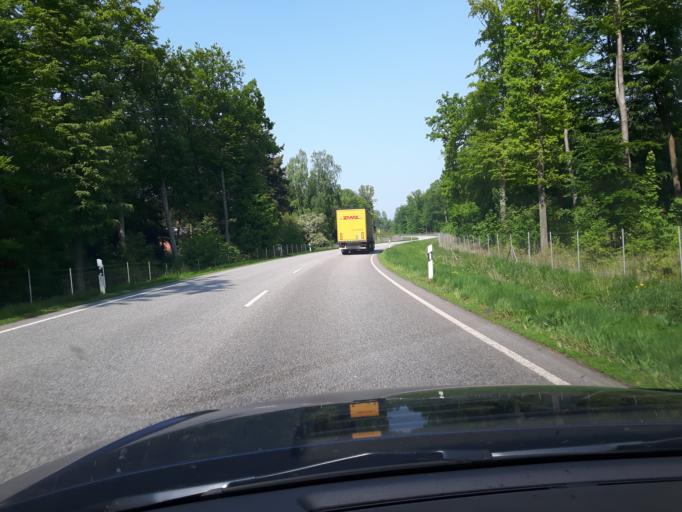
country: DE
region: Schleswig-Holstein
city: Ratekau
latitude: 53.8853
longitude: 10.7676
